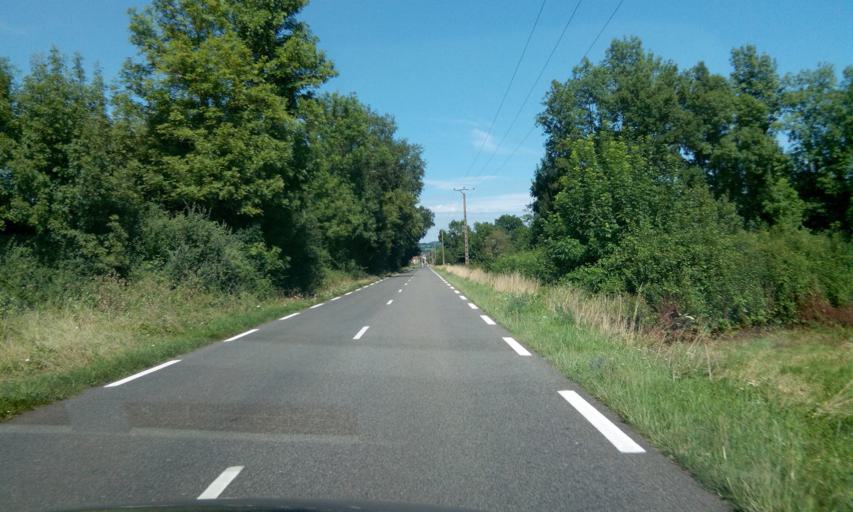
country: FR
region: Midi-Pyrenees
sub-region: Departement du Lot
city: Vayrac
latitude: 44.9456
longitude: 1.6840
